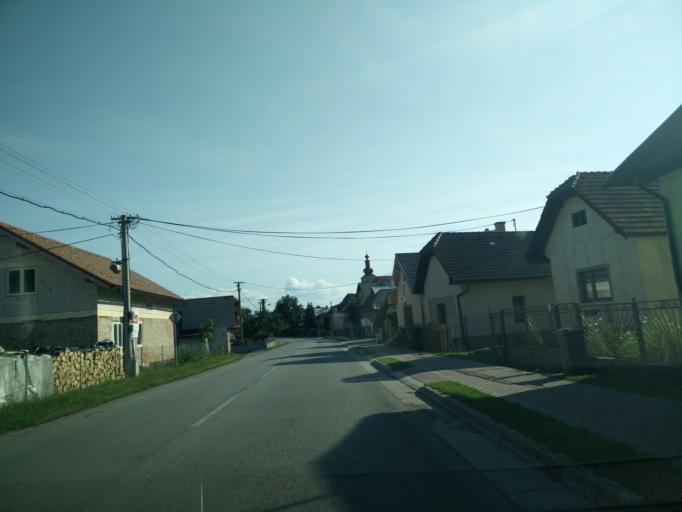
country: SK
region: Nitriansky
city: Handlova
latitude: 48.9111
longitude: 18.7598
